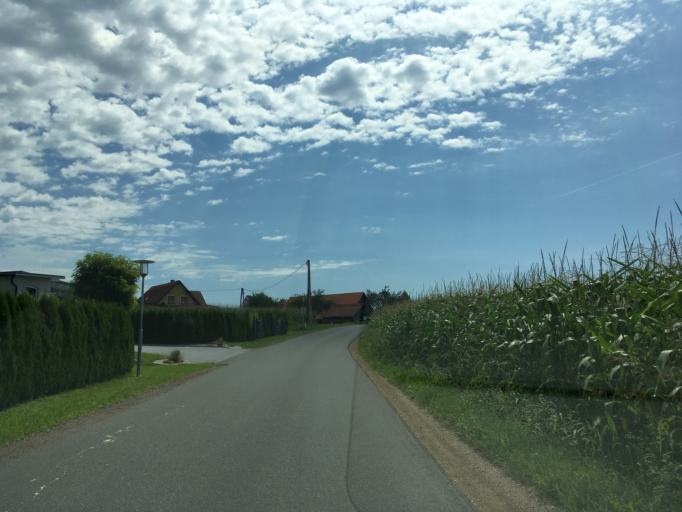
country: AT
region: Styria
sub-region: Politischer Bezirk Leibnitz
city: Gleinstatten
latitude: 46.7659
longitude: 15.3934
